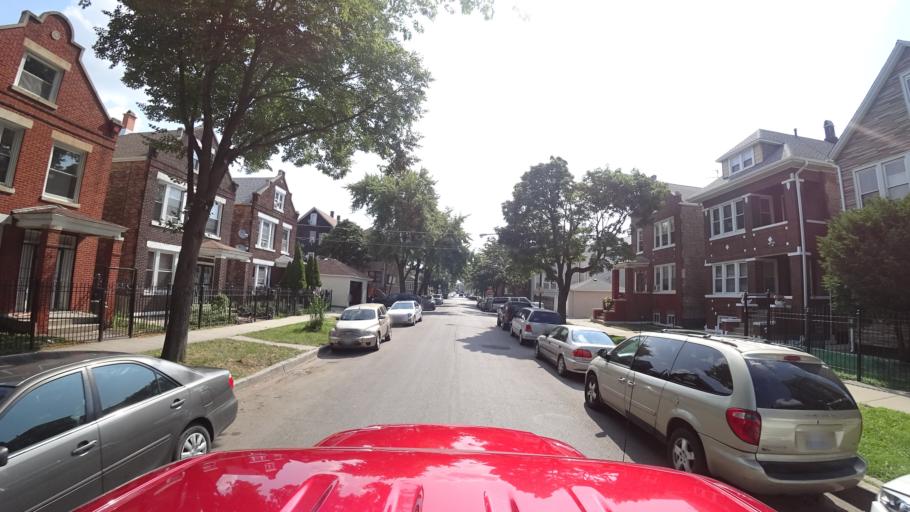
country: US
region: Illinois
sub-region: Cook County
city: Cicero
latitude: 41.8182
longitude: -87.7030
